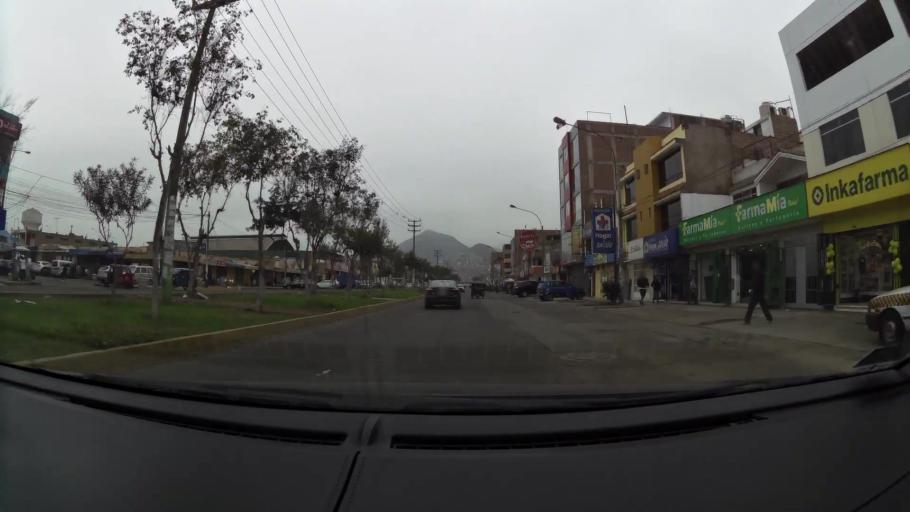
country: PE
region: Lima
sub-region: Lima
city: Independencia
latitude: -11.9720
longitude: -77.0711
